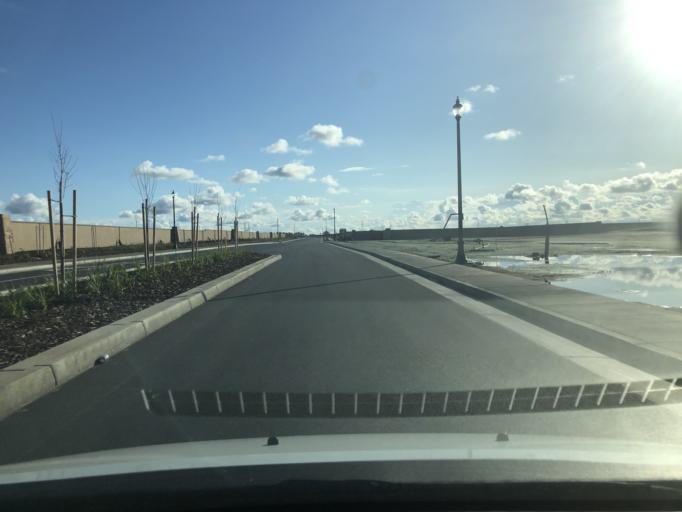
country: US
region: California
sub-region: Sacramento County
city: Elverta
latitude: 38.7749
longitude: -121.3967
